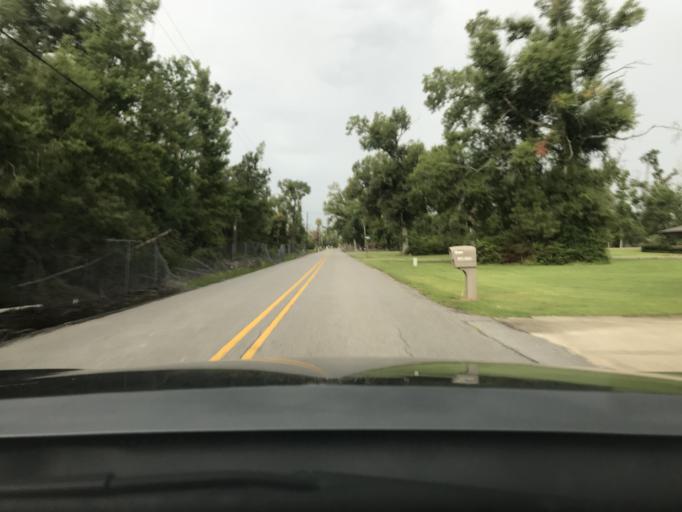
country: US
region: Louisiana
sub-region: Calcasieu Parish
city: Westlake
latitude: 30.2570
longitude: -93.2402
